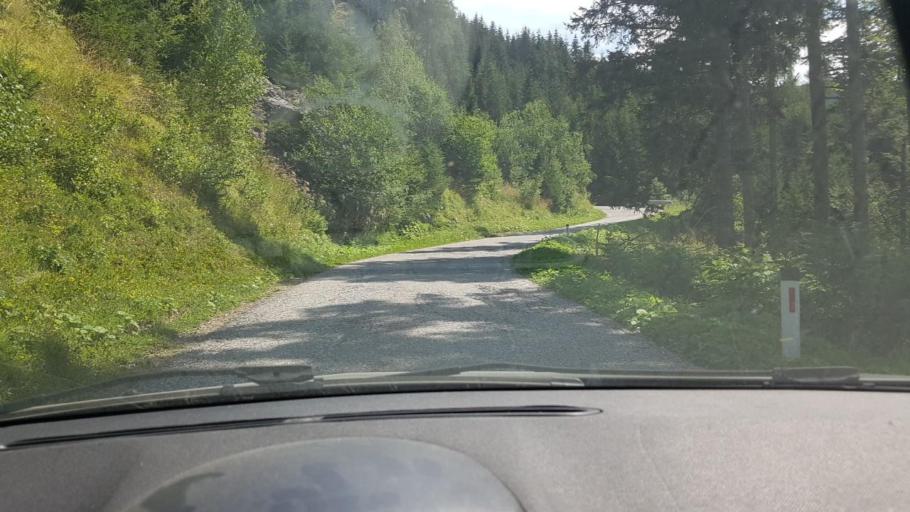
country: SI
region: Jezersko
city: Zgornje Jezersko
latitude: 46.4177
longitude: 14.5726
